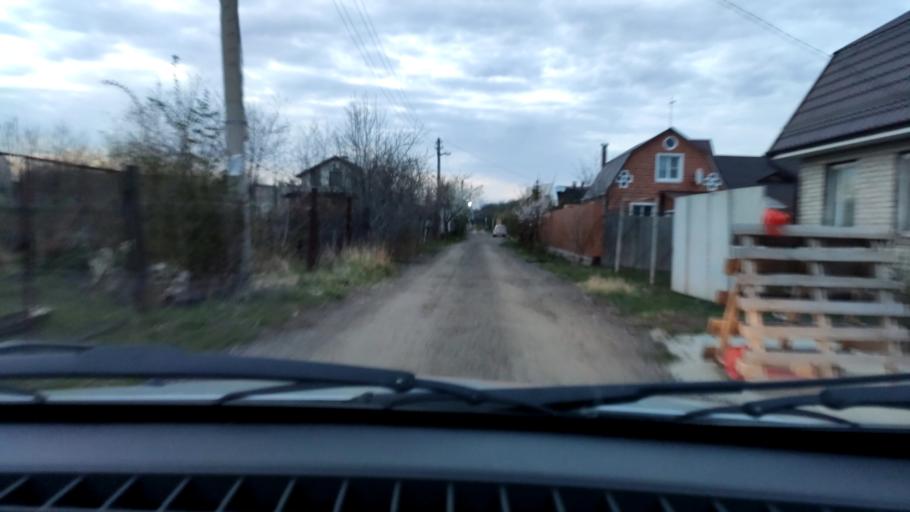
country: RU
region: Voronezj
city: Podgornoye
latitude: 51.7977
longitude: 39.2227
